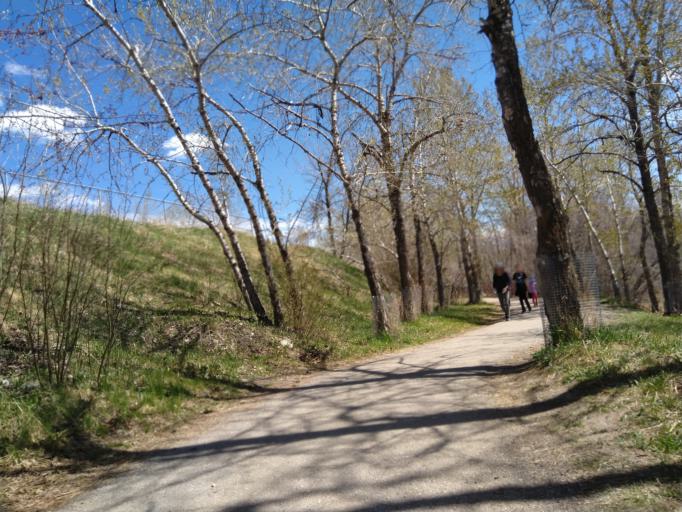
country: CA
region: Alberta
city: Calgary
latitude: 51.0998
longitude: -114.2057
